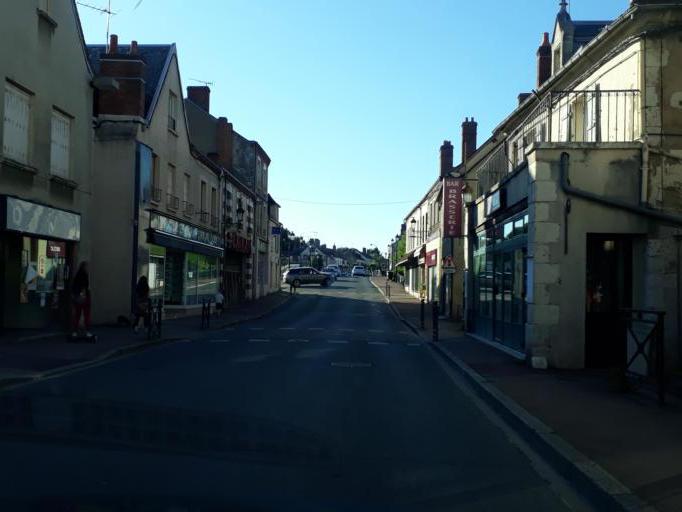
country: FR
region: Centre
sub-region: Departement du Loiret
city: Briare
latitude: 47.6393
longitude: 2.7381
